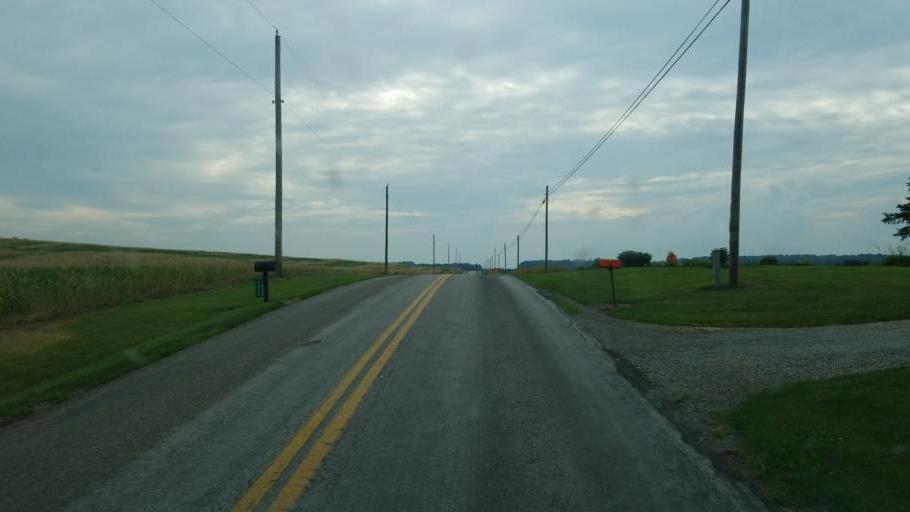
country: US
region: Ohio
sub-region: Wayne County
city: Apple Creek
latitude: 40.7557
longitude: -81.8062
